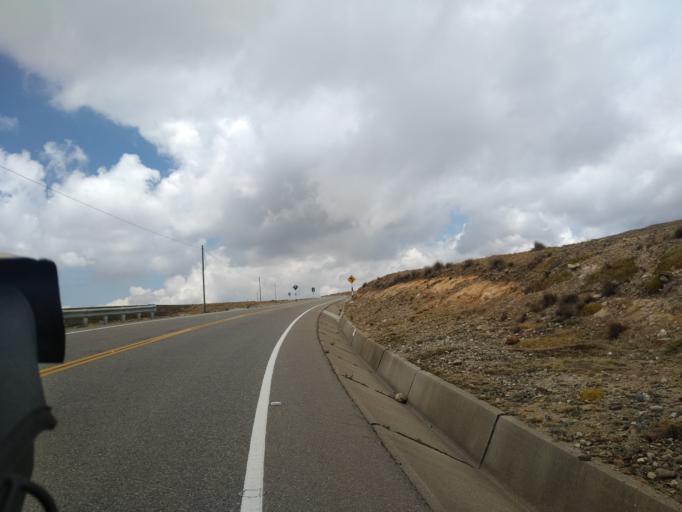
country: PE
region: La Libertad
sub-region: Provincia de Santiago de Chuco
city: Quiruvilca
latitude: -7.9642
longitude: -78.1980
